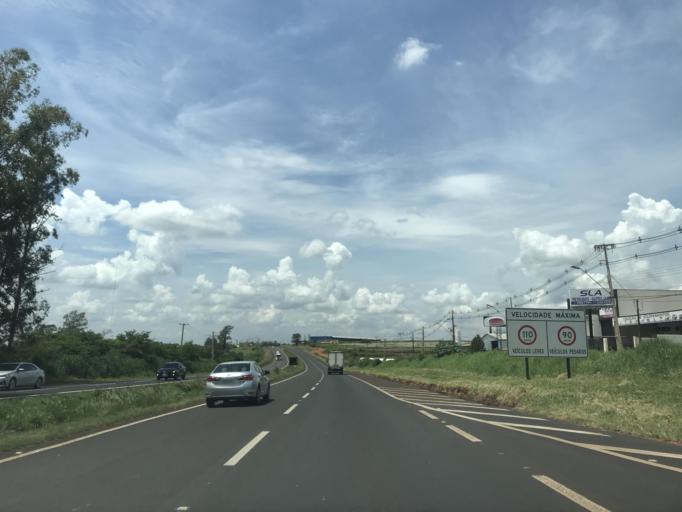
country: BR
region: Parana
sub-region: Alto Parana
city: Alto Parana
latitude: -23.2073
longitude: -52.1938
